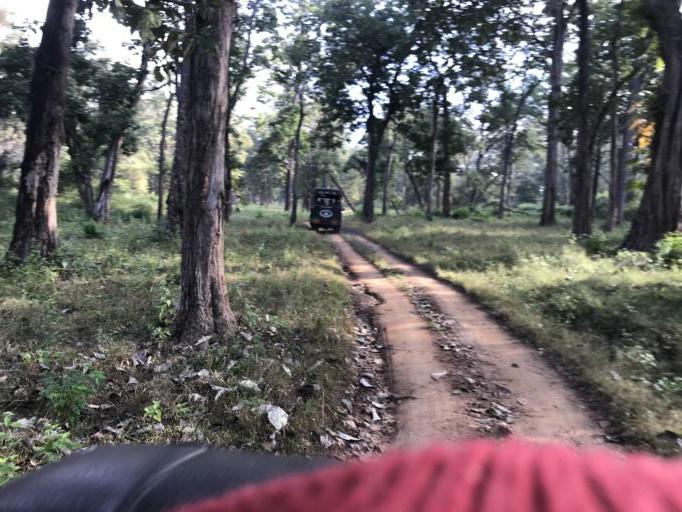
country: IN
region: Karnataka
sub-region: Mysore
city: Heggadadevankote
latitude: 11.9599
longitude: 76.2006
